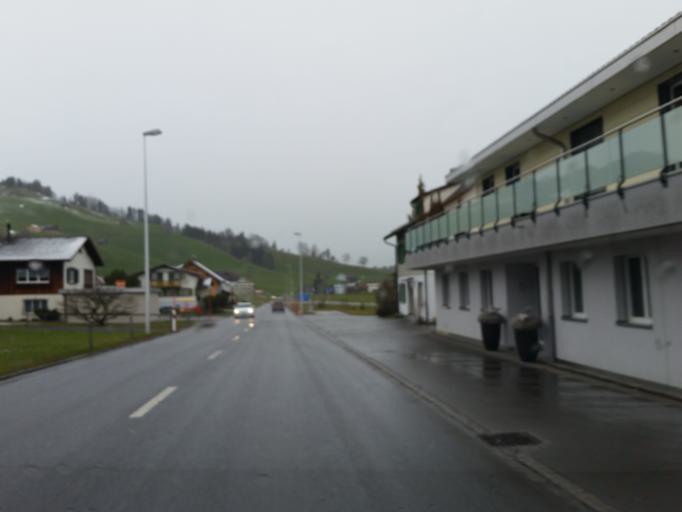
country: CH
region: Appenzell Innerrhoden
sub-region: Appenzell Inner Rhodes
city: Appenzell
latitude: 47.3324
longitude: 9.3964
